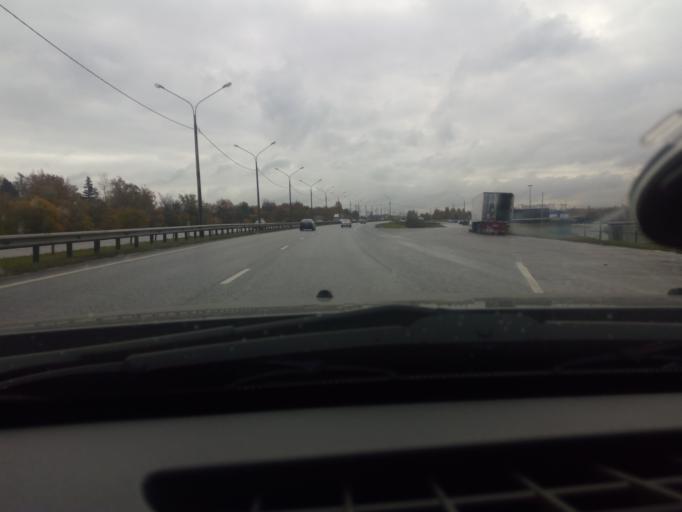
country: RU
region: Moskovskaya
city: Yam
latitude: 55.4740
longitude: 37.7438
